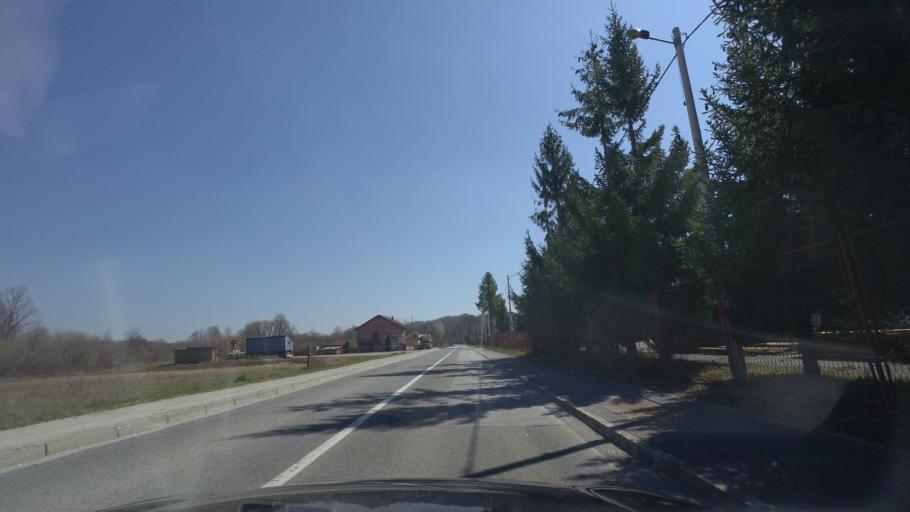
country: HR
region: Sisacko-Moslavacka
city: Gvozd
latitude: 45.3503
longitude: 15.8660
